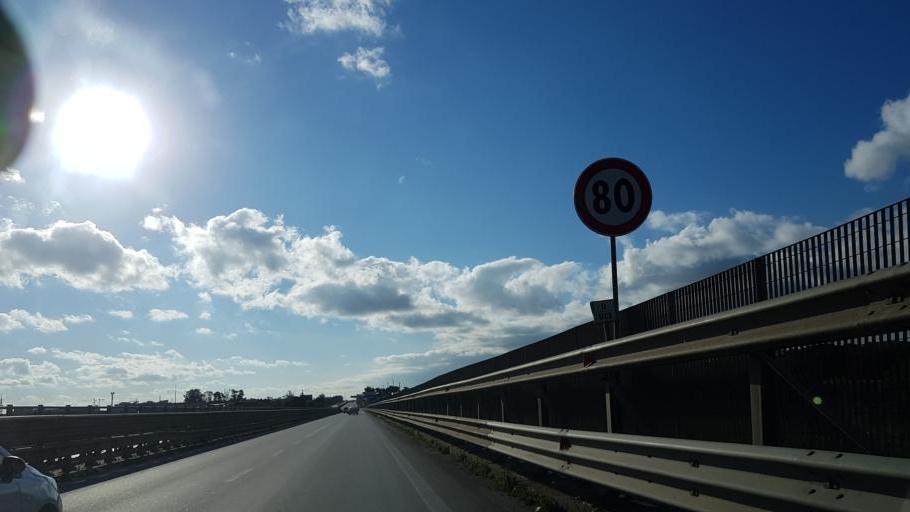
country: IT
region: Apulia
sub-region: Provincia di Brindisi
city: Brindisi
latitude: 40.6395
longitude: 17.9151
